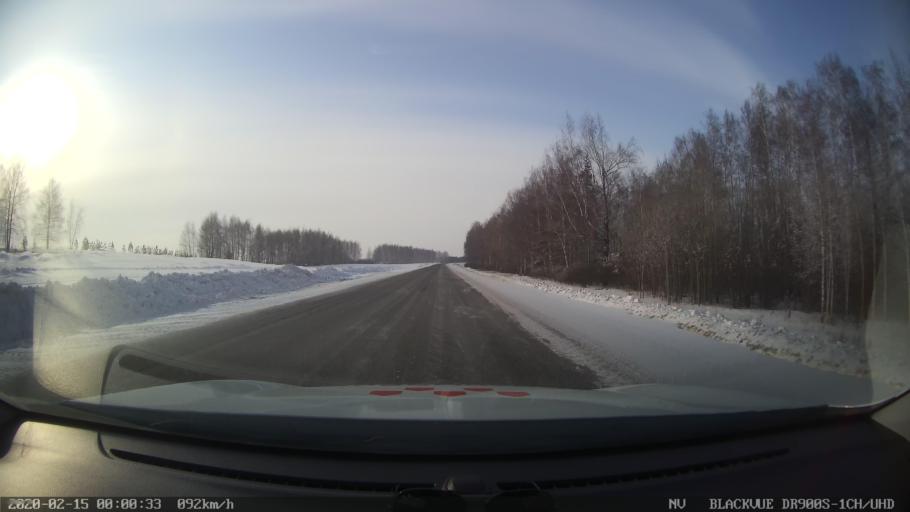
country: RU
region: Tatarstan
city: Kuybyshevskiy Zaton
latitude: 55.3437
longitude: 49.0362
